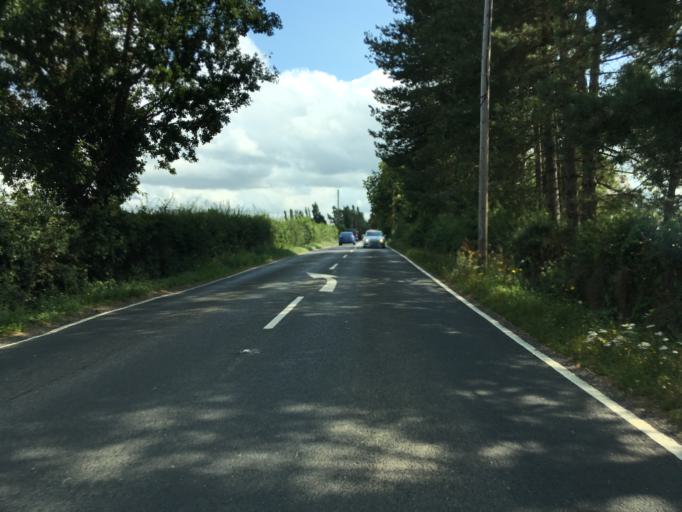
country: GB
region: England
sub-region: Kent
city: Headcorn
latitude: 51.1472
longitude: 0.6391
